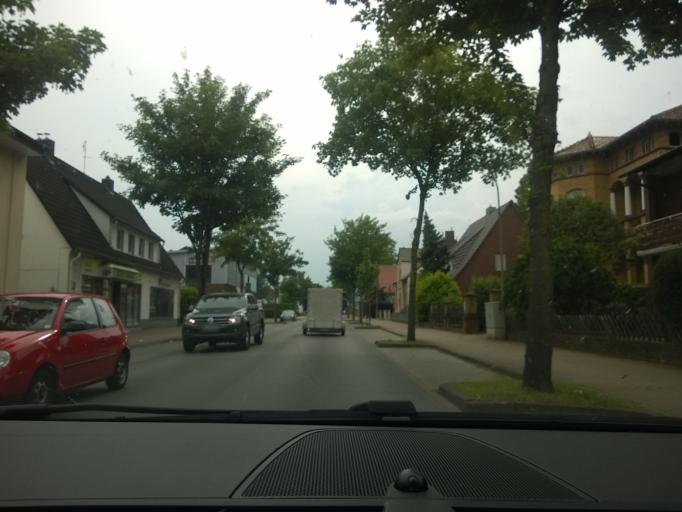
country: DE
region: North Rhine-Westphalia
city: Stadtlohn
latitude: 51.9893
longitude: 6.9136
